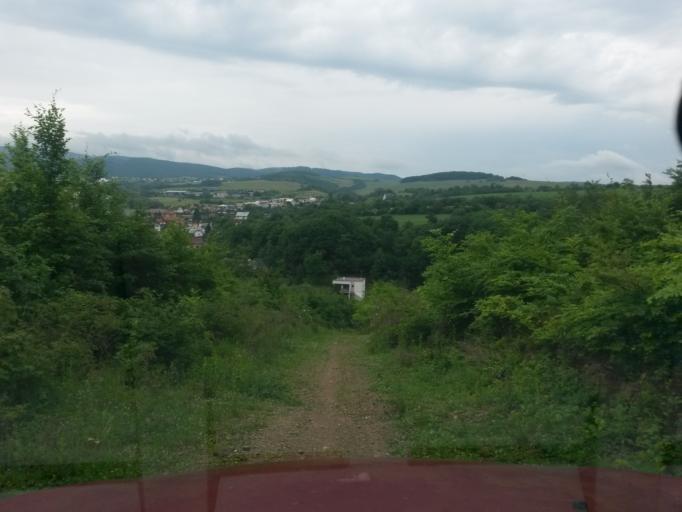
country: SK
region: Kosicky
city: Kosice
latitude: 48.7234
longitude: 21.1466
